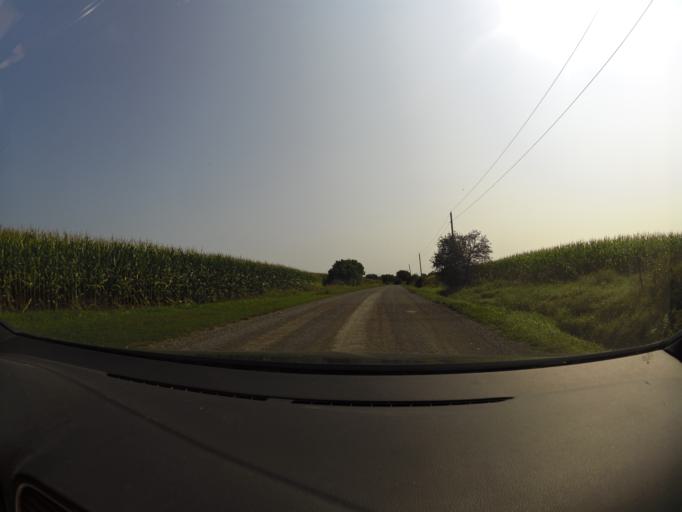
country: CA
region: Ontario
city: Carleton Place
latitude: 45.3546
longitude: -76.0849
